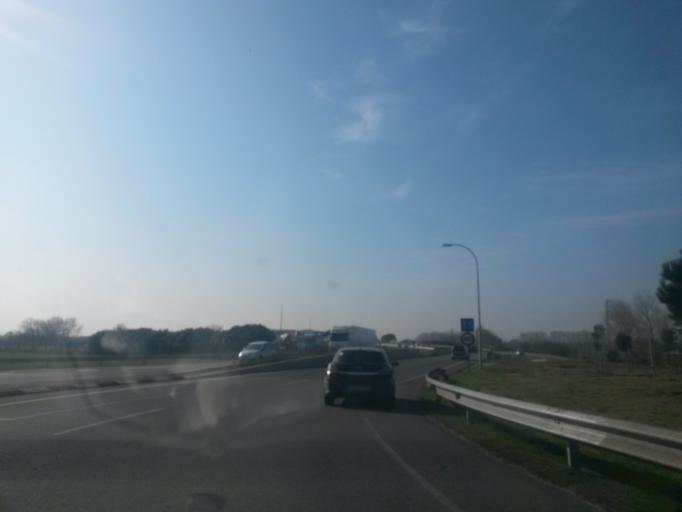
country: ES
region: Catalonia
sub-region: Provincia de Girona
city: Castello d'Empuries
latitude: 42.2605
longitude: 3.0935
